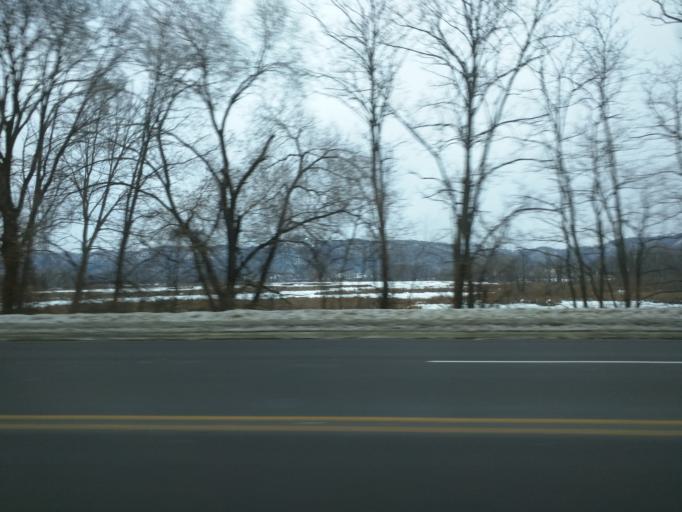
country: US
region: Wisconsin
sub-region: La Crosse County
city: La Crosse
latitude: 43.8239
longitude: -91.2399
